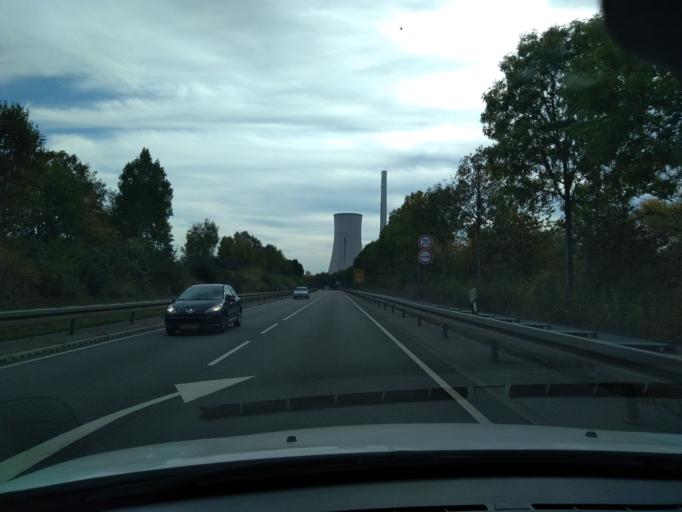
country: DE
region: Saarland
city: Ensdorf
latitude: 49.3012
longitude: 6.7725
